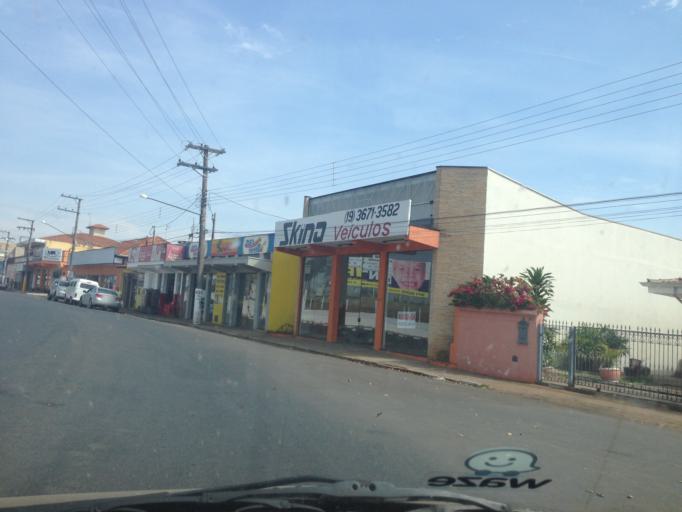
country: BR
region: Sao Paulo
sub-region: Casa Branca
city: Casa Branca
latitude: -21.7782
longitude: -47.0771
